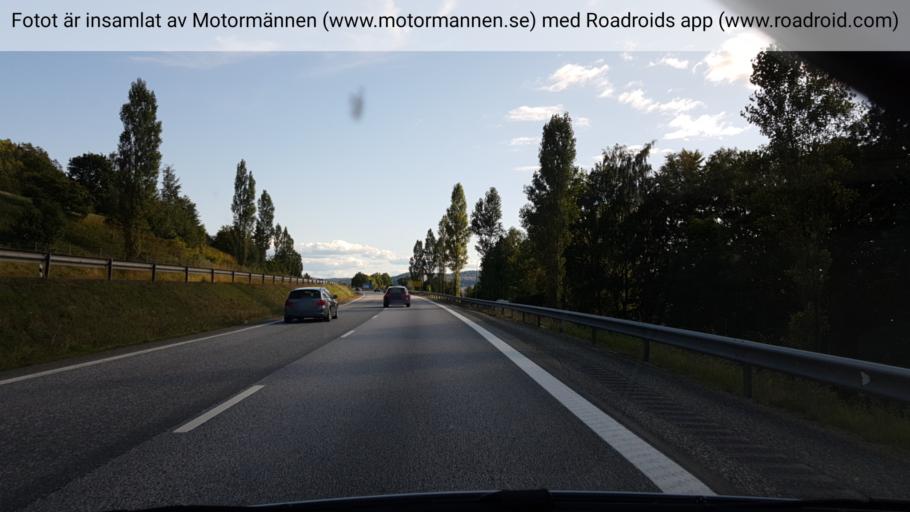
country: SE
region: Joenkoeping
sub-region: Jonkopings Kommun
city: Kaxholmen
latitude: 57.8258
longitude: 14.2696
